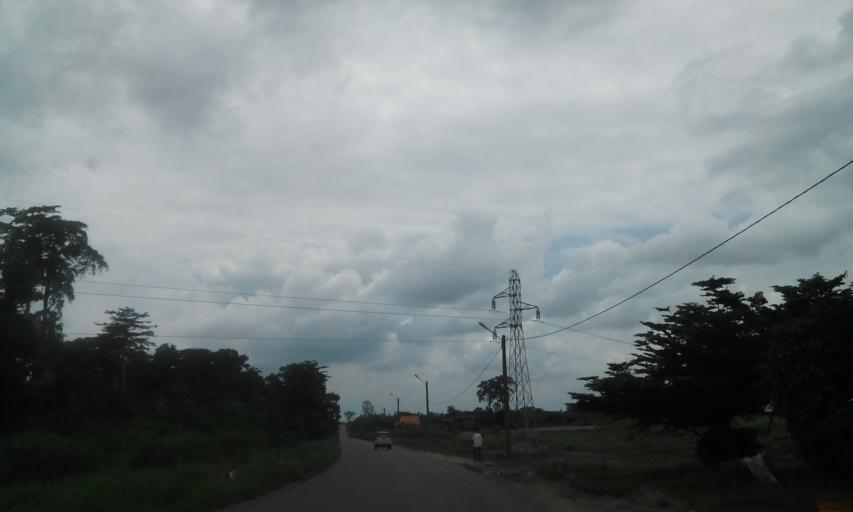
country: CI
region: Sud-Comoe
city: Aboisso
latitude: 5.4296
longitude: -3.2646
